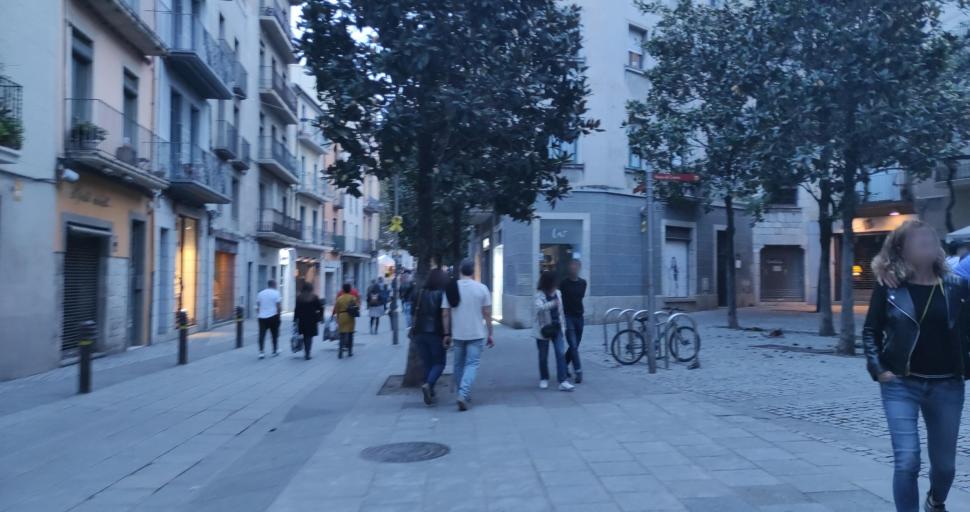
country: ES
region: Catalonia
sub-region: Provincia de Girona
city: Girona
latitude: 41.9840
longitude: 2.8231
